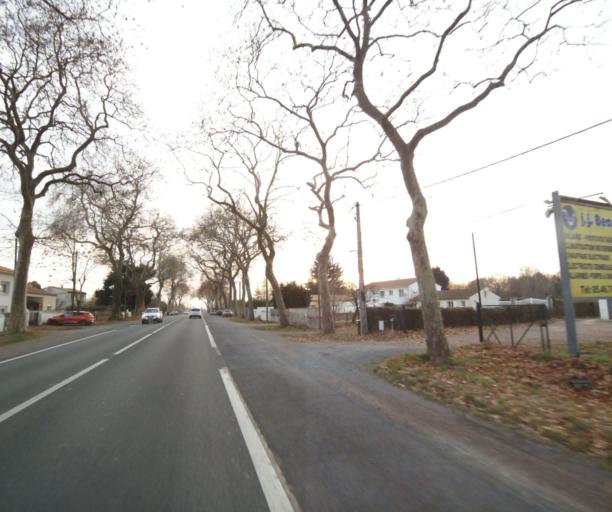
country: FR
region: Poitou-Charentes
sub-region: Departement de la Charente-Maritime
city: Fontcouverte
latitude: 45.7620
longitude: -0.5871
